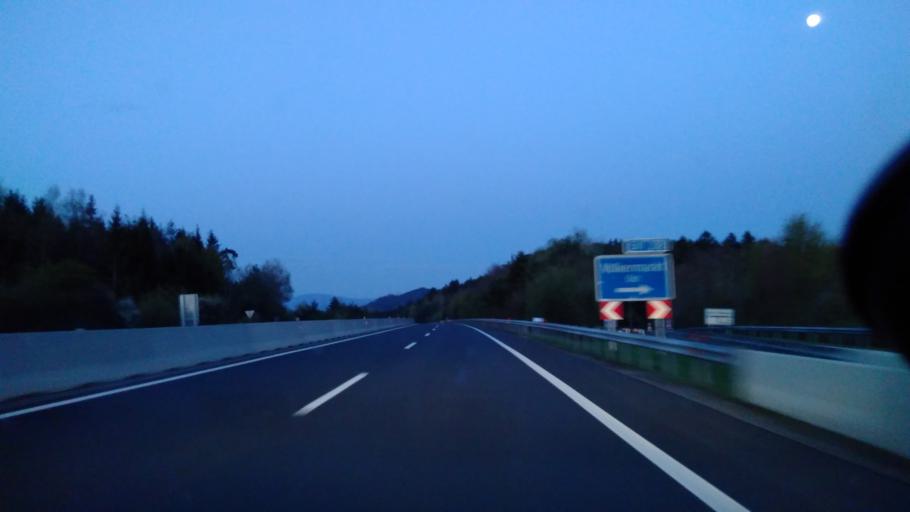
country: AT
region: Carinthia
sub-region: Politischer Bezirk Volkermarkt
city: Voelkermarkt
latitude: 46.6829
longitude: 14.6769
